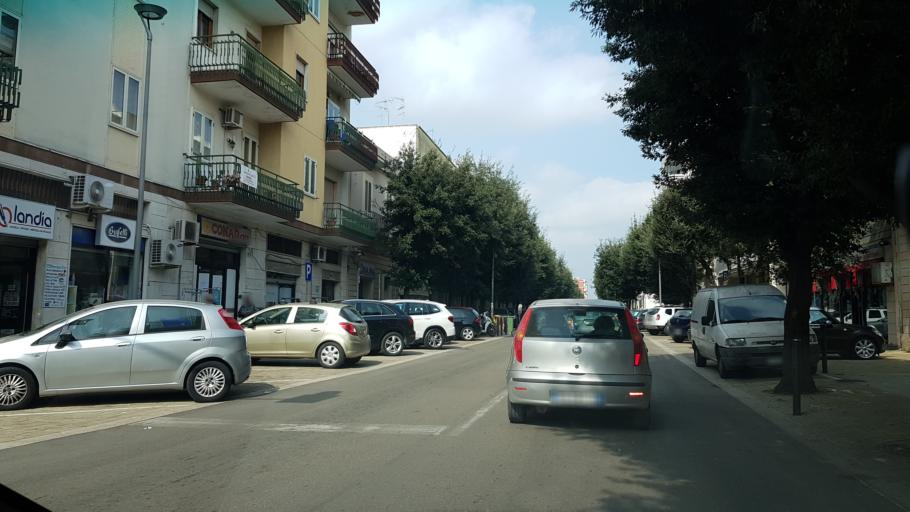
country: IT
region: Apulia
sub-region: Provincia di Lecce
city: Castromediano
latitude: 40.3394
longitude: 18.1769
